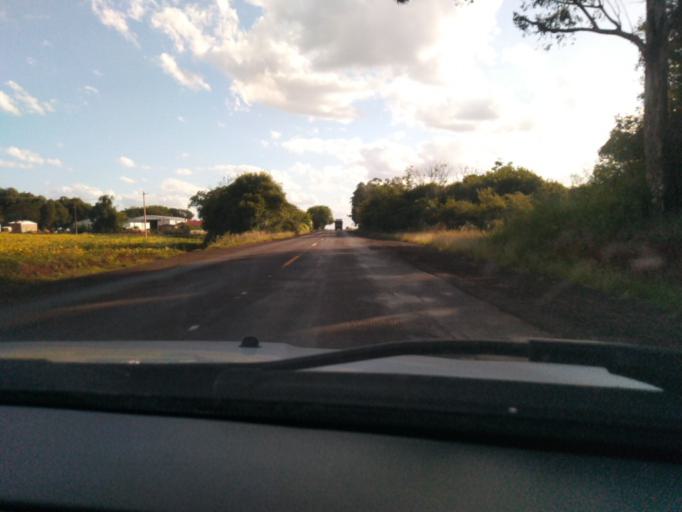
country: AR
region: Corrientes
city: Garruchos
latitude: -28.5503
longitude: -55.5657
